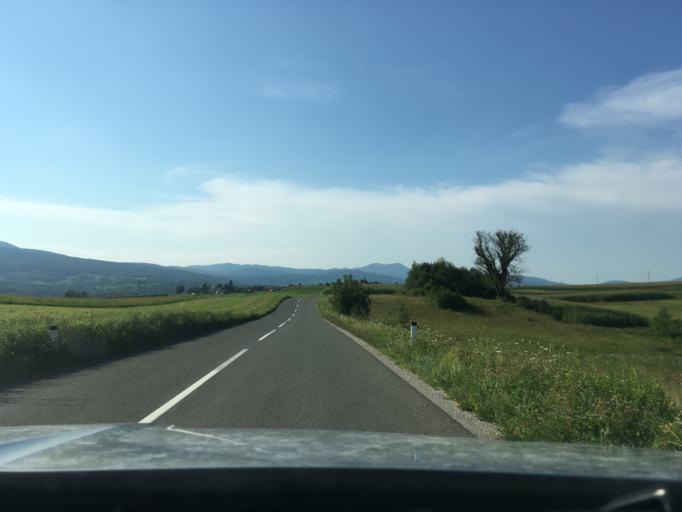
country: SI
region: Crnomelj
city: Crnomelj
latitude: 45.5138
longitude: 15.1839
